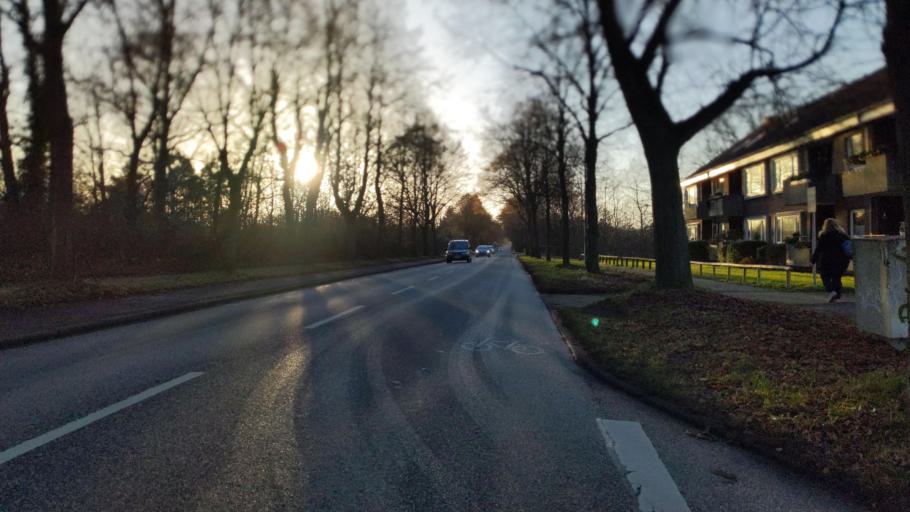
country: DE
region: Mecklenburg-Vorpommern
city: Selmsdorf
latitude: 53.8844
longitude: 10.7867
